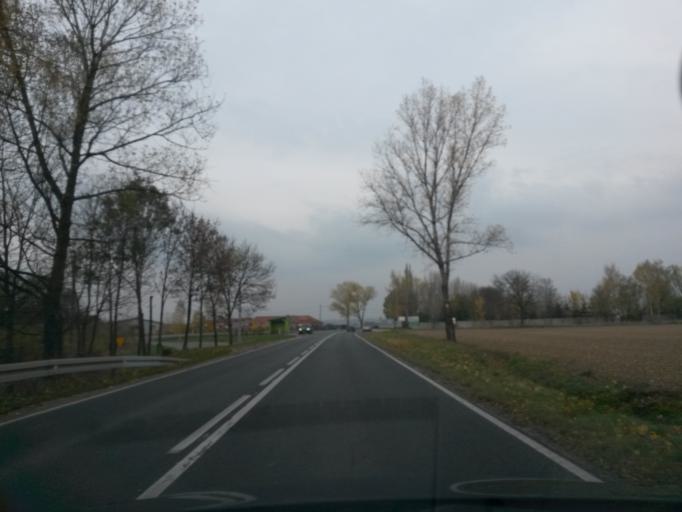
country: PL
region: Lower Silesian Voivodeship
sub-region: Powiat klodzki
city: Klodzko
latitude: 50.3892
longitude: 16.6603
